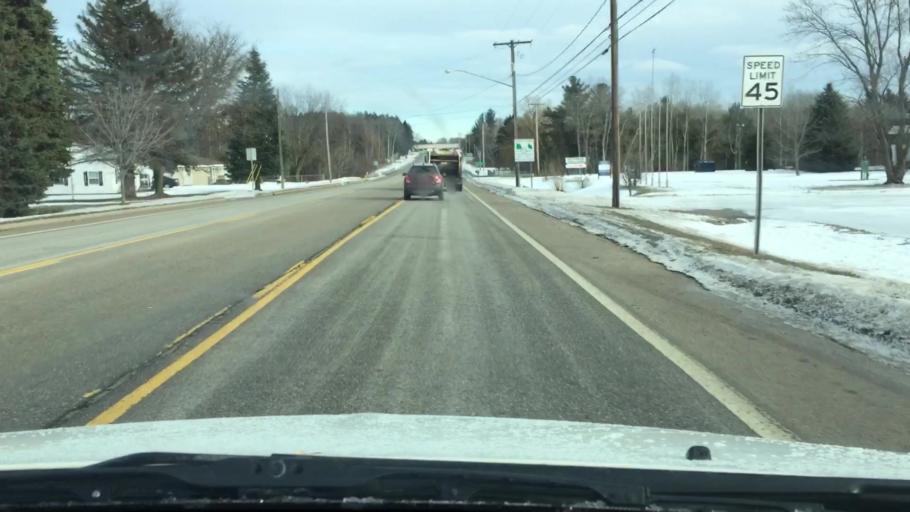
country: US
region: Michigan
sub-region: Wexford County
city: Manton
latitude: 44.4036
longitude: -85.3952
